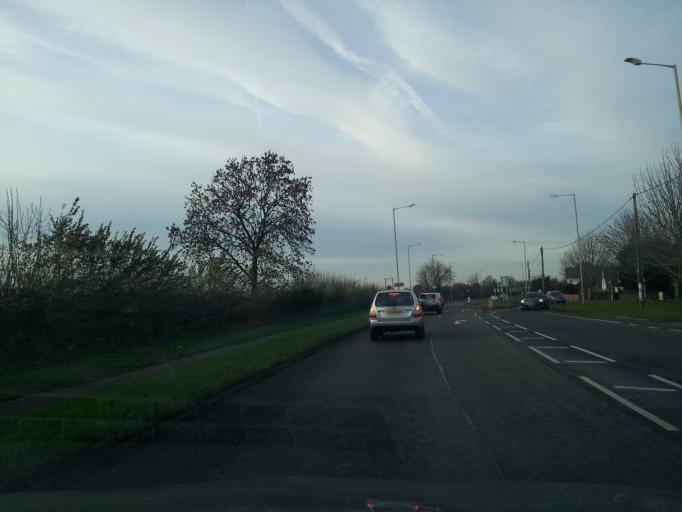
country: GB
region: England
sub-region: Buckinghamshire
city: Weston Turville
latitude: 51.7848
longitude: -0.7760
